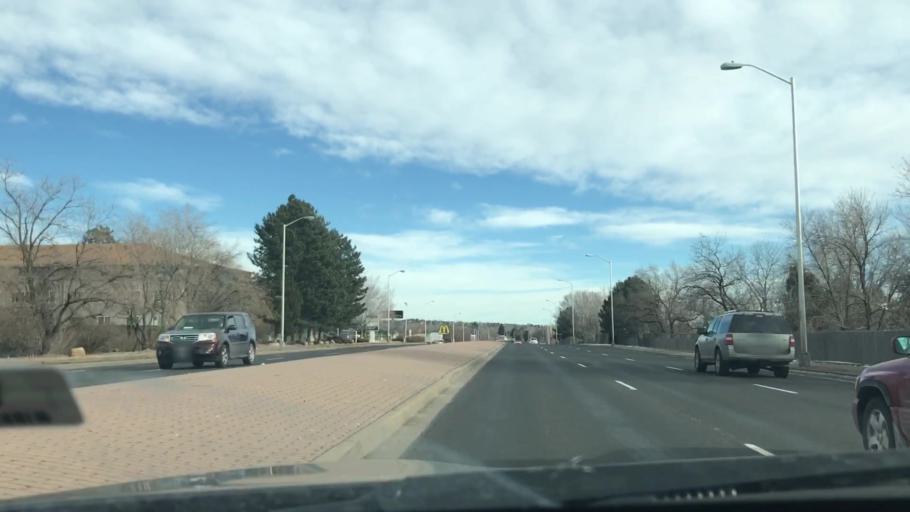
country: US
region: Colorado
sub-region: El Paso County
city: Colorado Springs
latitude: 38.9030
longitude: -104.7720
